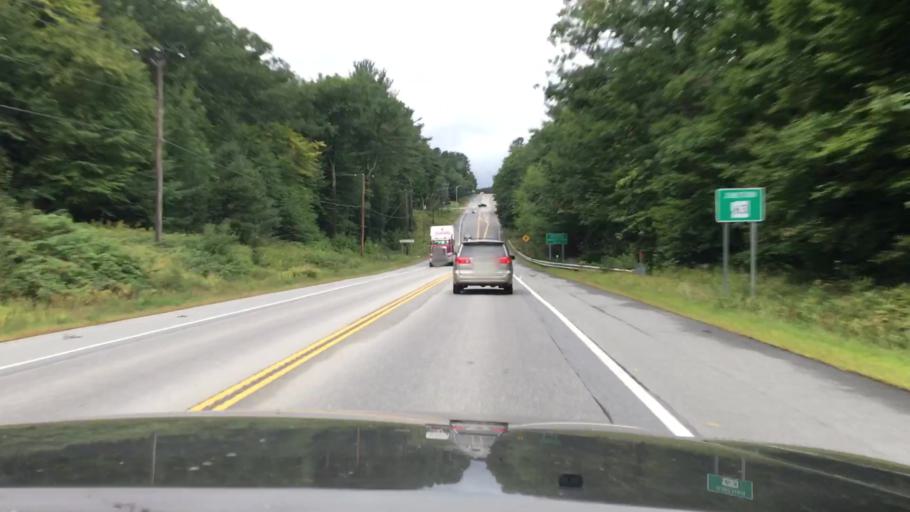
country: US
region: New Hampshire
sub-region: Cheshire County
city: Chesterfield
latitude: 42.8998
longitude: -72.4543
